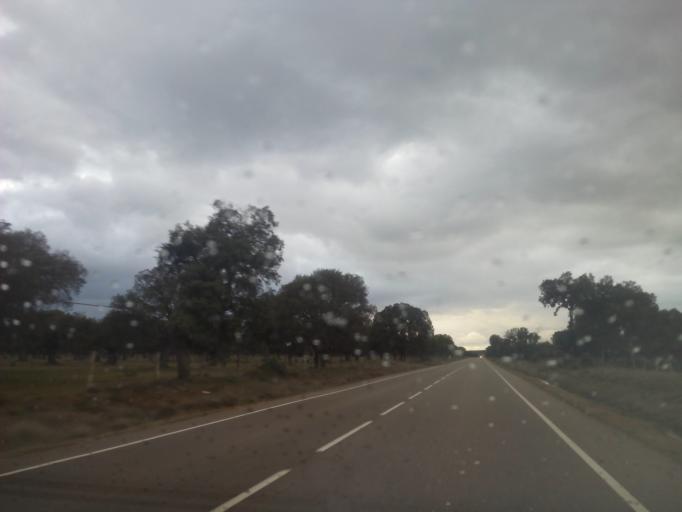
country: ES
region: Castille and Leon
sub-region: Provincia de Salamanca
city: Abusejo
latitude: 40.7244
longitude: -6.1538
